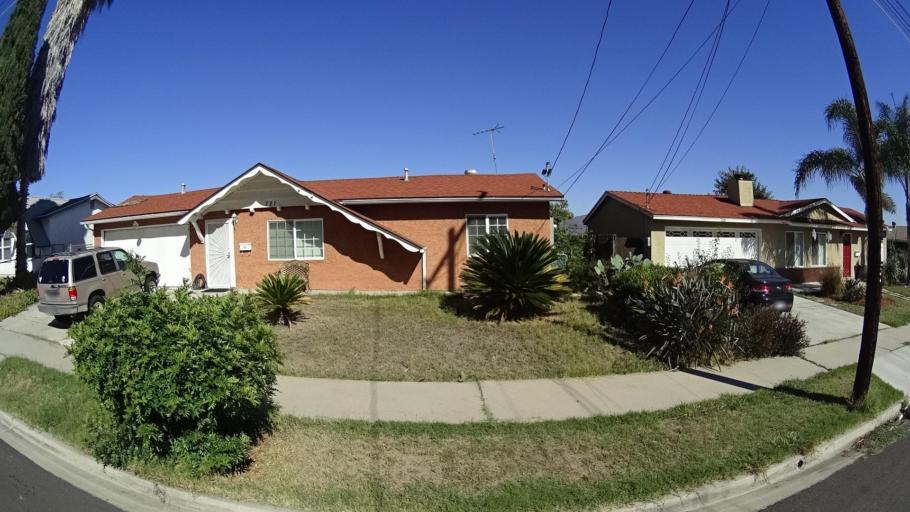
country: US
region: California
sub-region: San Diego County
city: La Presa
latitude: 32.7064
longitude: -117.0196
